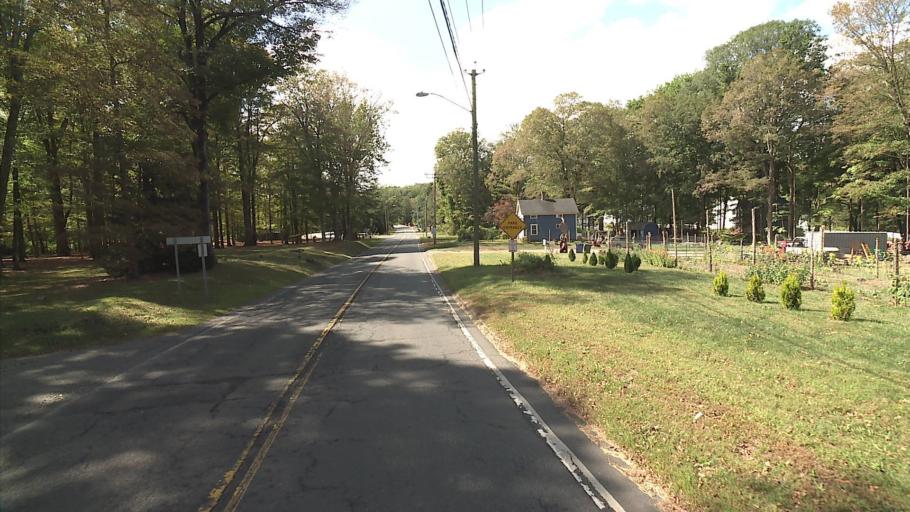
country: US
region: Connecticut
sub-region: Middlesex County
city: Middletown
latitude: 41.5378
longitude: -72.6842
